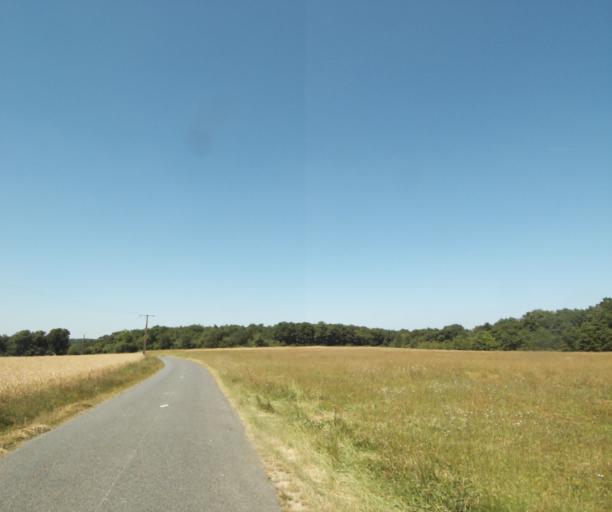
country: FR
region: Ile-de-France
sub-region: Departement de Seine-et-Marne
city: Noisy-sur-Ecole
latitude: 48.3138
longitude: 2.5014
